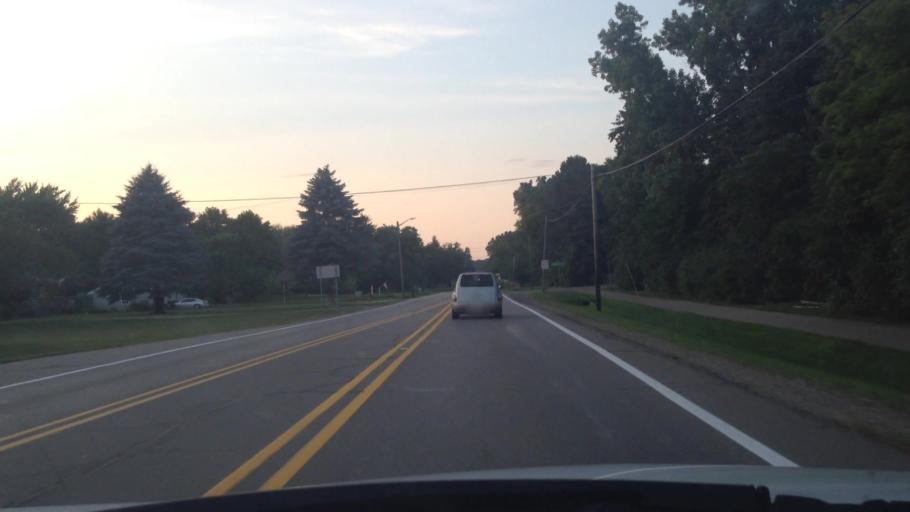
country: US
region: Michigan
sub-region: Oakland County
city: Lake Orion
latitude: 42.7368
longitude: -83.3080
